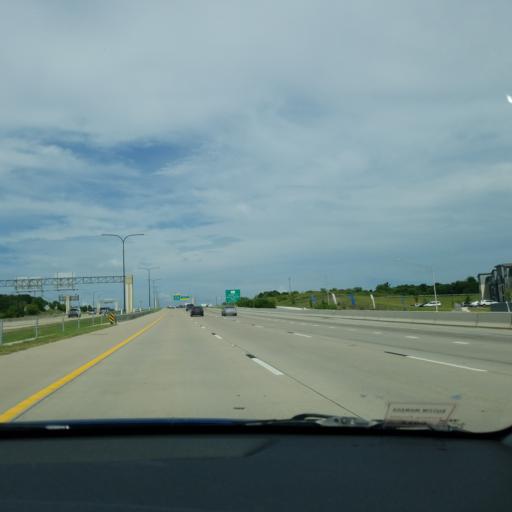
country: US
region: Texas
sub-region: Travis County
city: Manor
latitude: 30.3295
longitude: -97.6408
